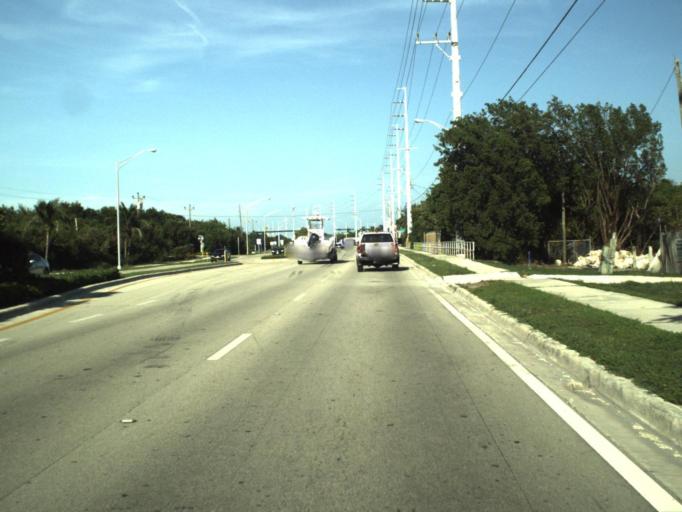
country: US
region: Florida
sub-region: Monroe County
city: Marathon
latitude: 24.7315
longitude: -81.0236
